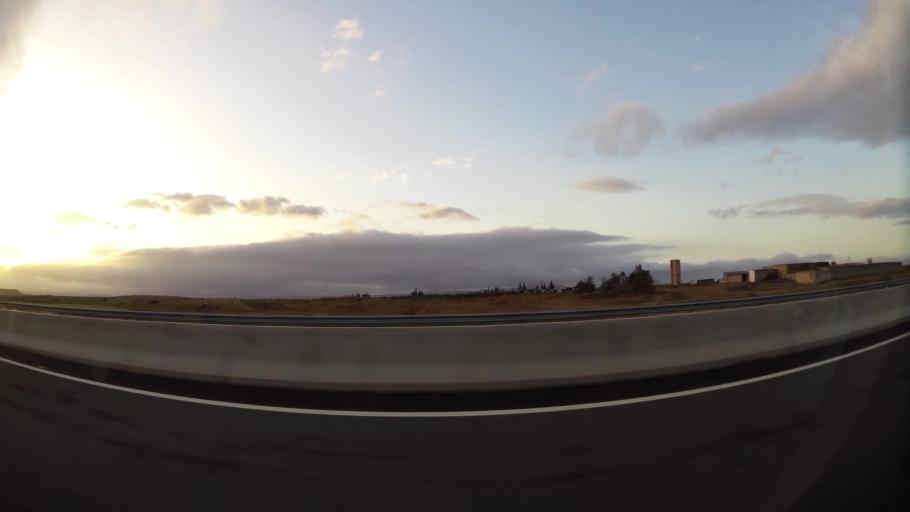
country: MA
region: Oriental
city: Taourirt
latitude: 34.5502
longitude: -2.8668
